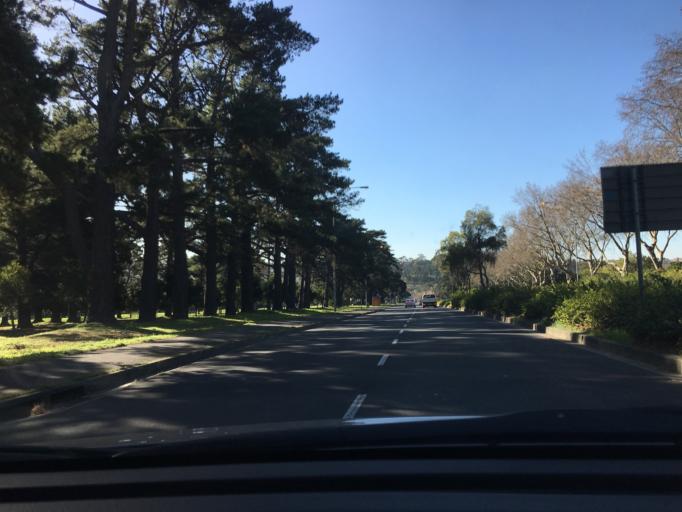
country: ZA
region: Western Cape
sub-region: City of Cape Town
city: Bergvliet
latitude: -34.0186
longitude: 18.4485
